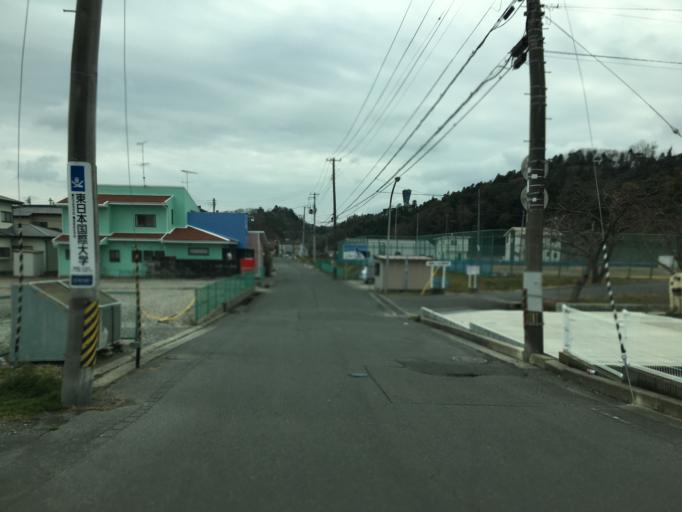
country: JP
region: Fukushima
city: Iwaki
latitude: 36.9468
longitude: 140.9244
